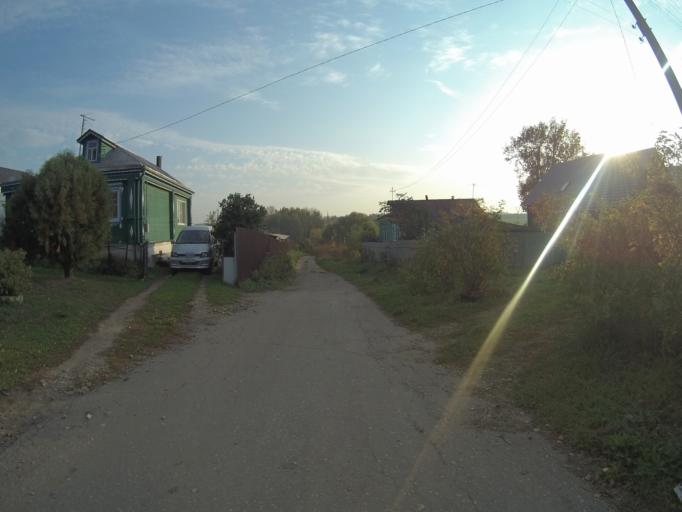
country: RU
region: Vladimir
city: Bogolyubovo
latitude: 56.1896
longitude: 40.4905
